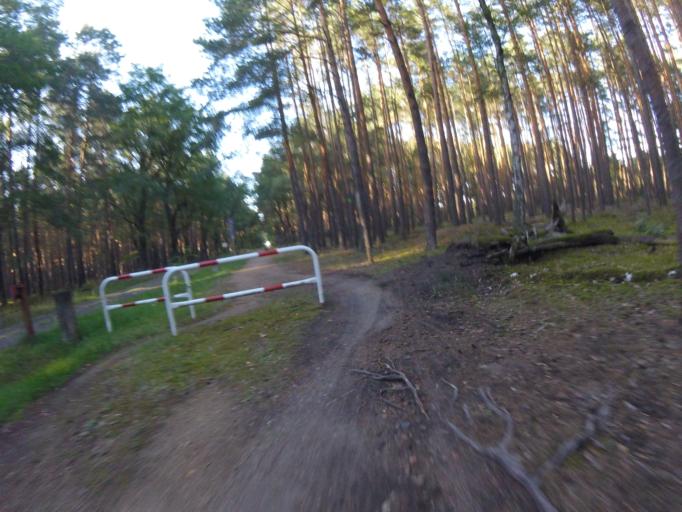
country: DE
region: Brandenburg
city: Munchehofe
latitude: 52.2123
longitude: 13.7719
